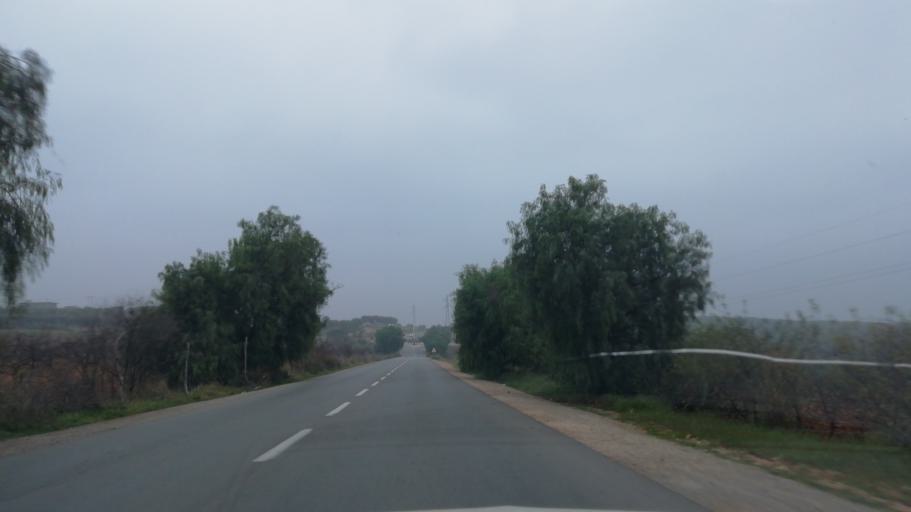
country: DZ
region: Mascara
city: Mascara
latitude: 35.4016
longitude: 0.1638
